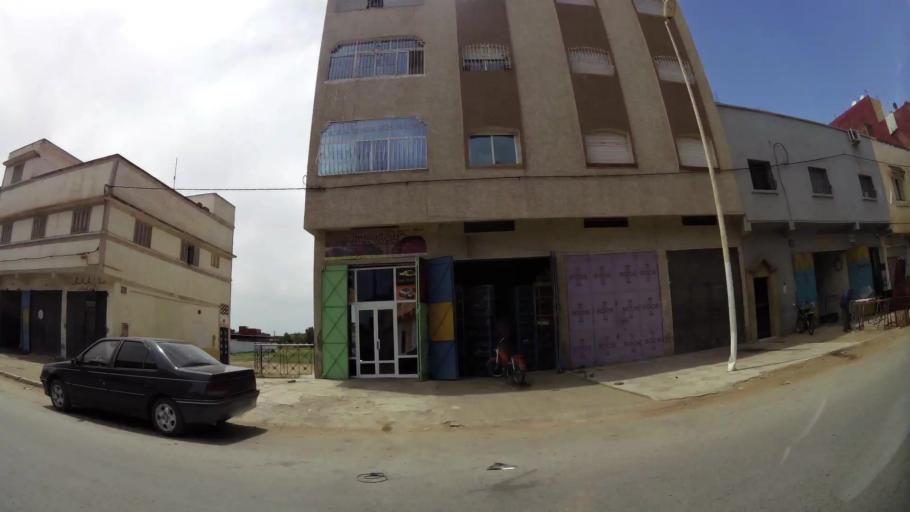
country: MA
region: Rabat-Sale-Zemmour-Zaer
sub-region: Khemisset
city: Khemisset
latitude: 33.8223
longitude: -6.0769
